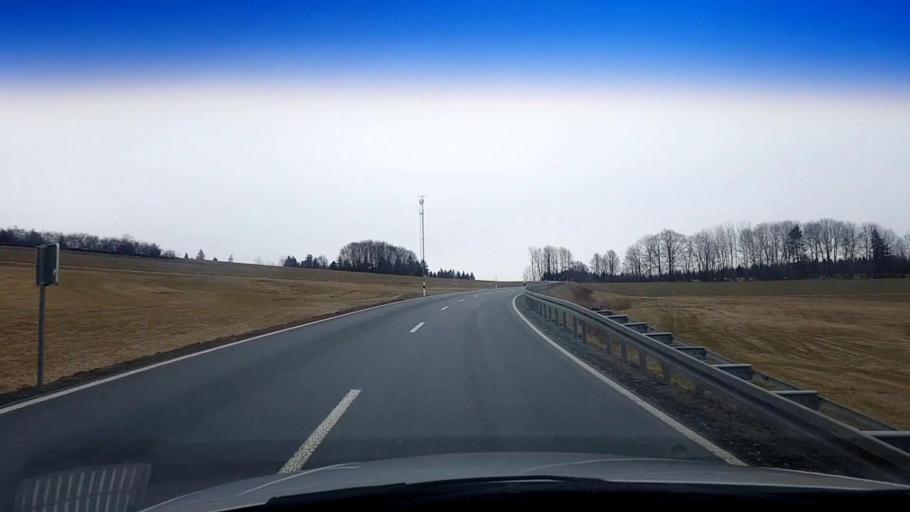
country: DE
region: Bavaria
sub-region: Upper Franconia
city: Kupferberg
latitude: 50.1496
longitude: 11.5851
